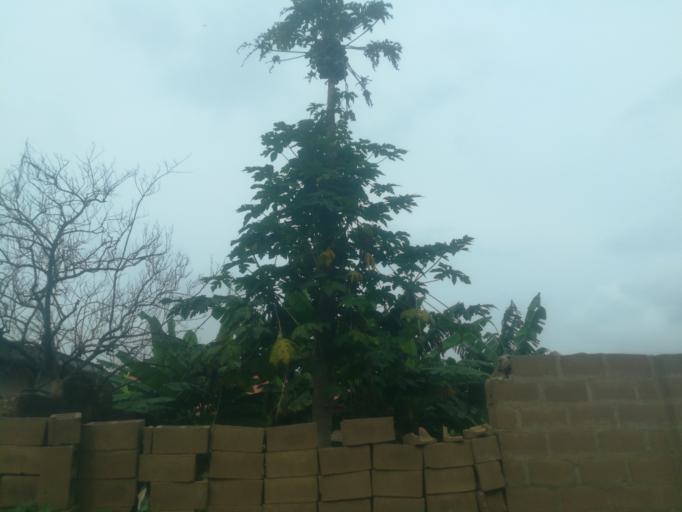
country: NG
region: Oyo
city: Ibadan
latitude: 7.4140
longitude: 3.9416
